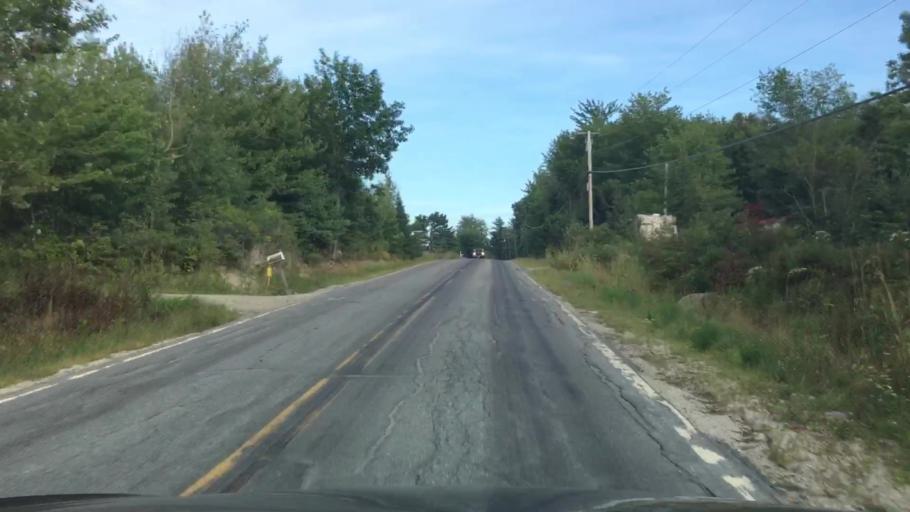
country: US
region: Maine
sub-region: Hancock County
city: Surry
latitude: 44.5056
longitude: -68.5906
